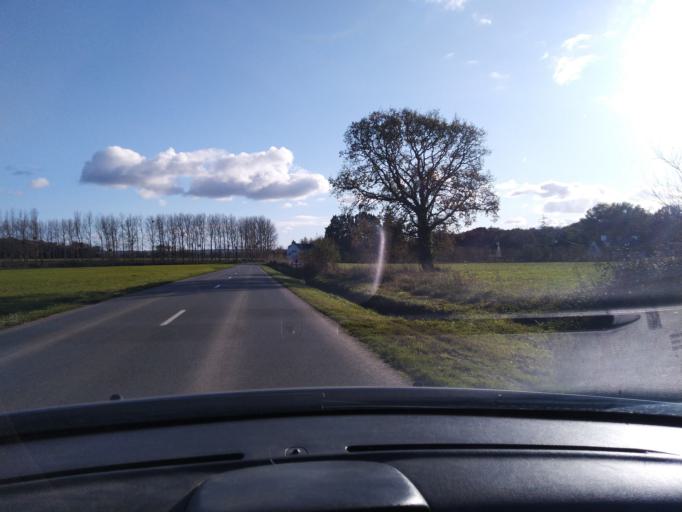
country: FR
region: Brittany
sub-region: Departement des Cotes-d'Armor
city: Plestin-les-Greves
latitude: 48.6290
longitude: -3.6156
